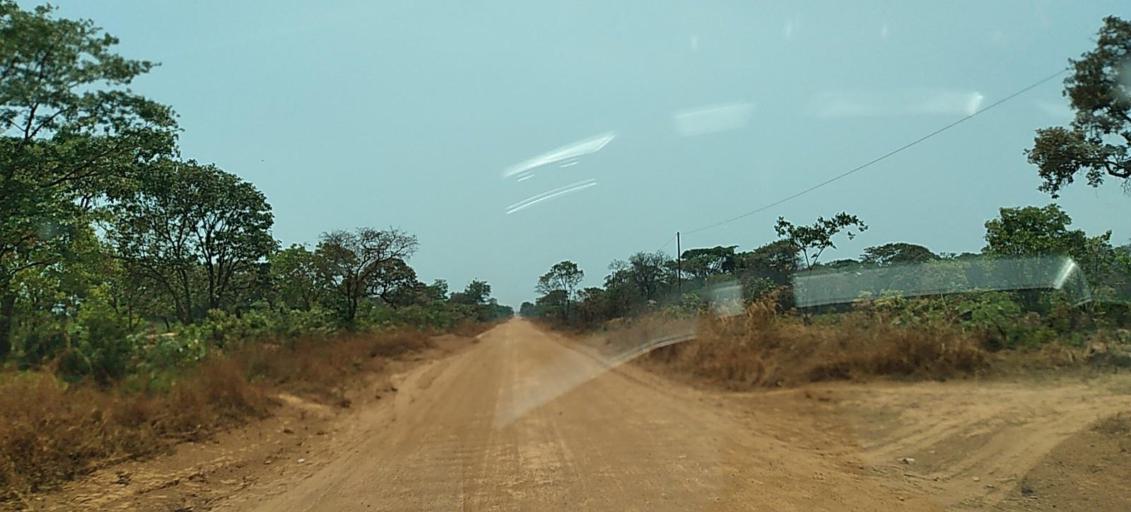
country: CD
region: Katanga
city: Kipushi
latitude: -11.9320
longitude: 26.9775
